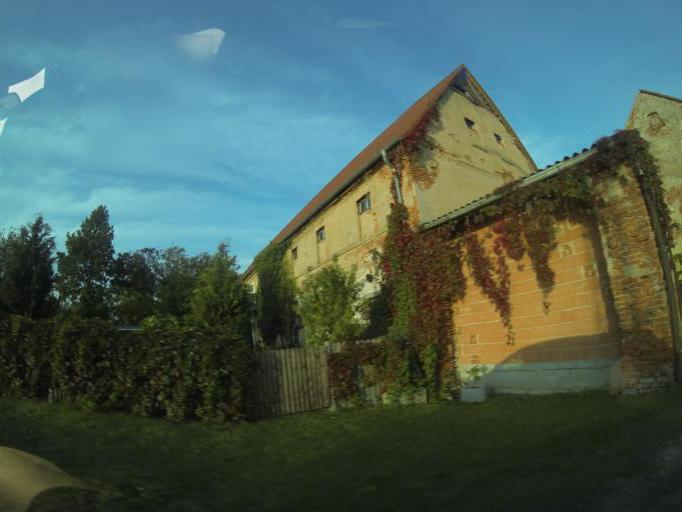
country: DE
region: Thuringia
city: Altkirchen
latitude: 50.9326
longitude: 12.3597
